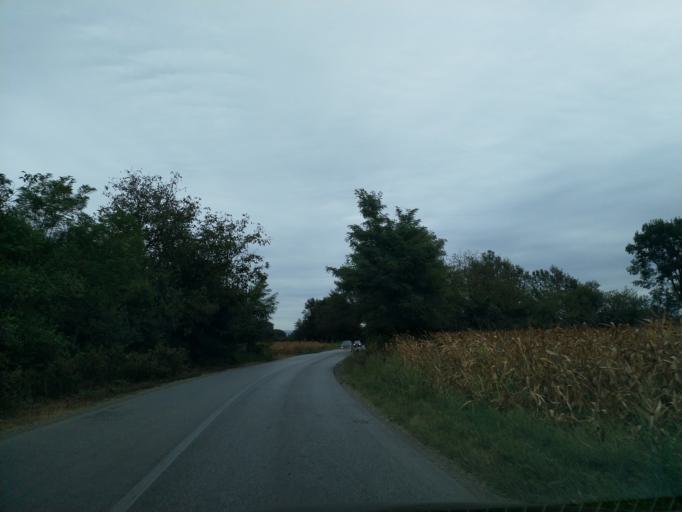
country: RS
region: Central Serbia
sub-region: Pomoravski Okrug
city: Paracin
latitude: 43.8376
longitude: 21.3705
